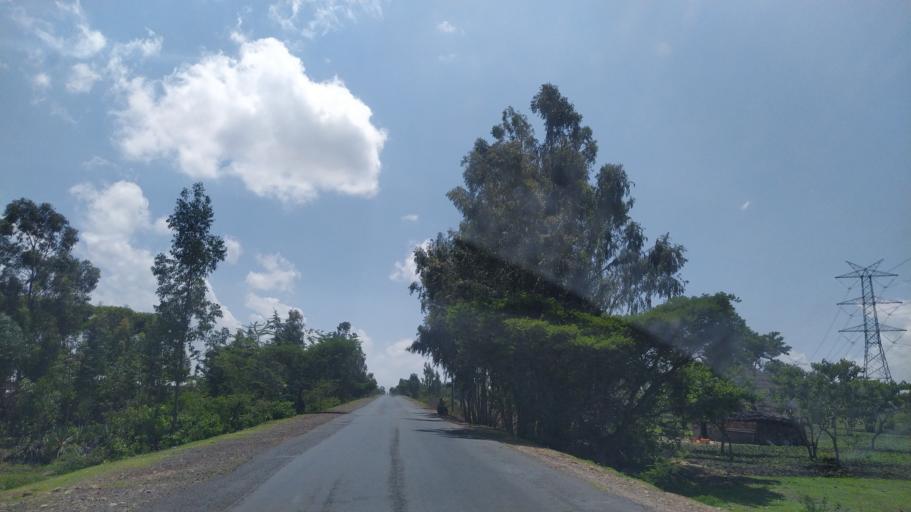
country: ET
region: Southern Nations, Nationalities, and People's Region
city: Butajira
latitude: 7.7561
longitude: 38.1307
